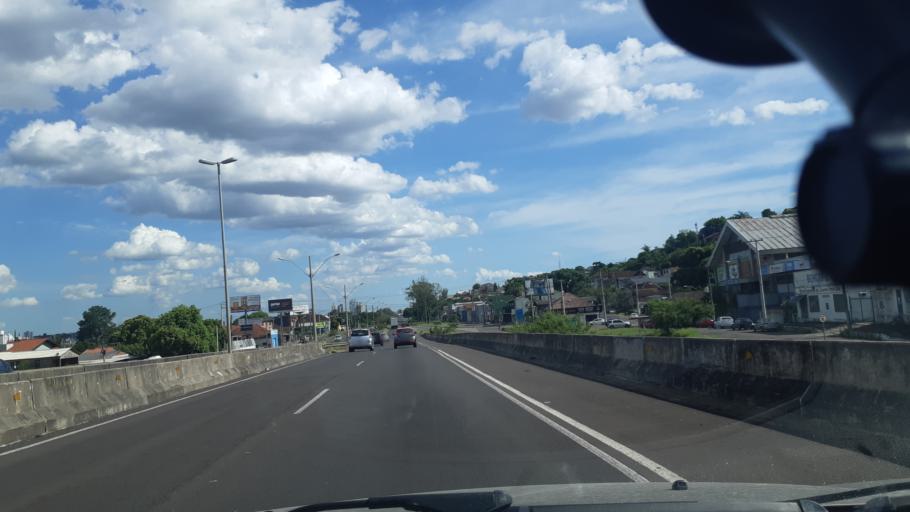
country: BR
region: Rio Grande do Sul
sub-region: Novo Hamburgo
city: Novo Hamburgo
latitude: -29.6709
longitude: -51.1431
